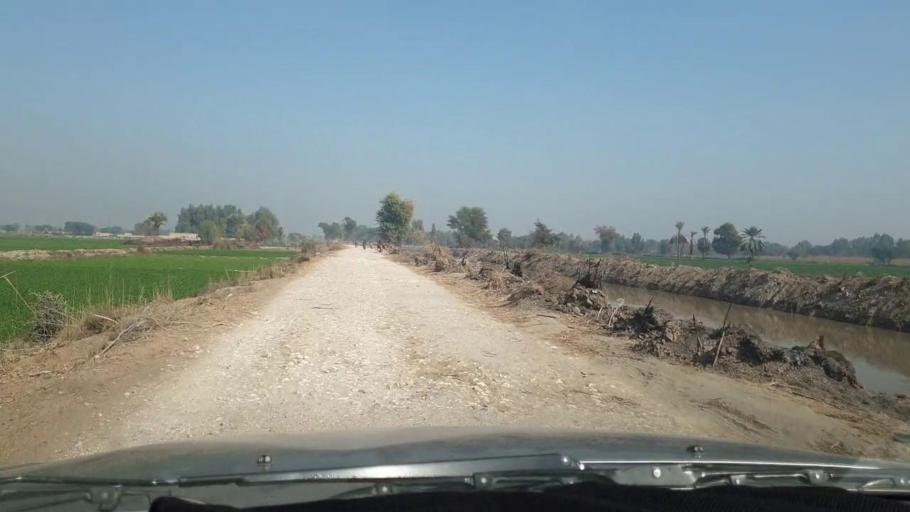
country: PK
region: Sindh
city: Khanpur
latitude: 27.7955
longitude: 69.5653
